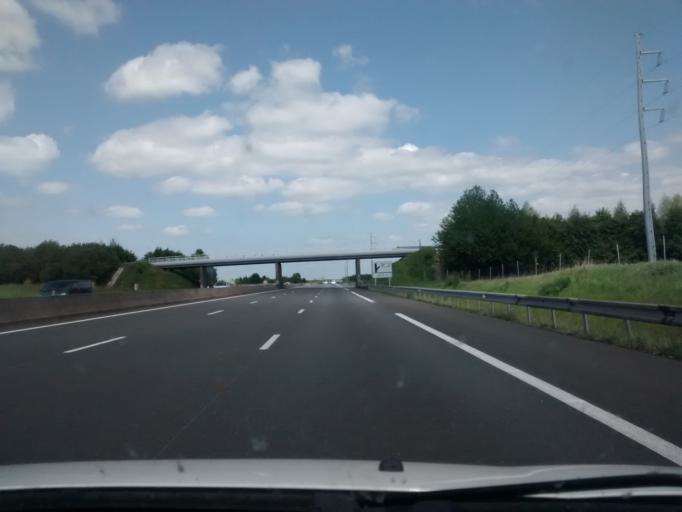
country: FR
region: Centre
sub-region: Departement d'Eure-et-Loir
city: Dammarie
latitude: 48.3525
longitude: 1.4253
